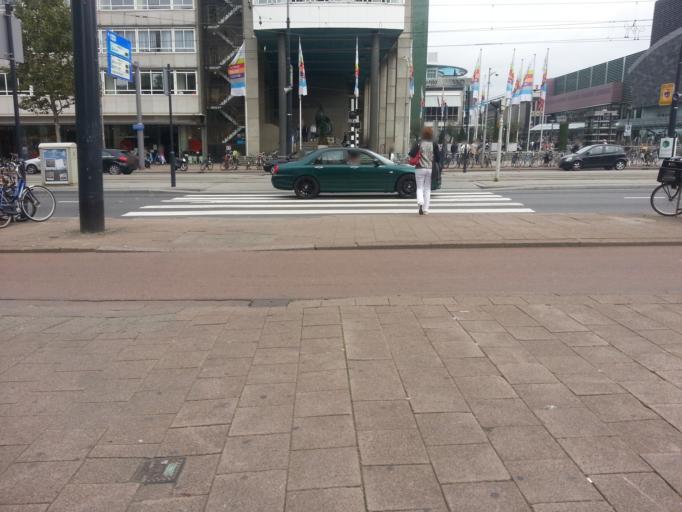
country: NL
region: South Holland
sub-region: Gemeente Rotterdam
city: Rotterdam
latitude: 51.9202
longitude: 4.4796
